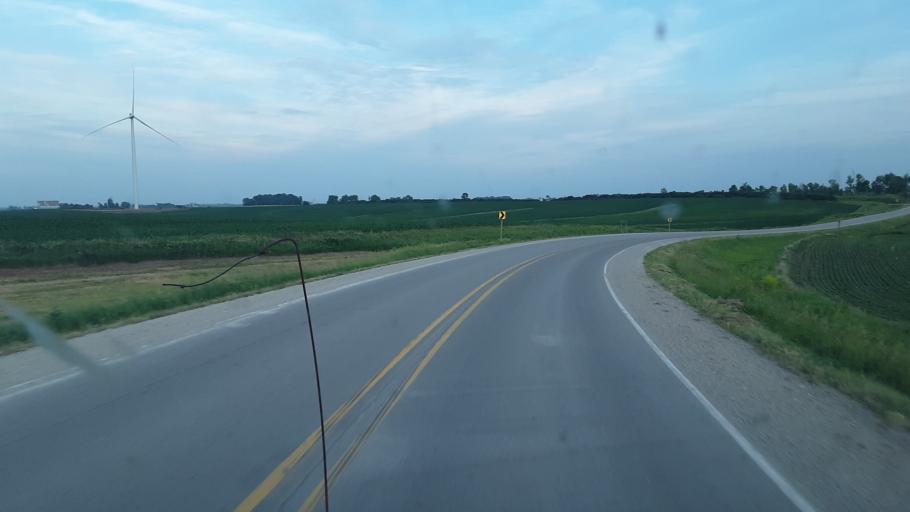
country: US
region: Iowa
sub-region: Iowa County
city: Marengo
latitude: 41.7018
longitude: -92.1629
